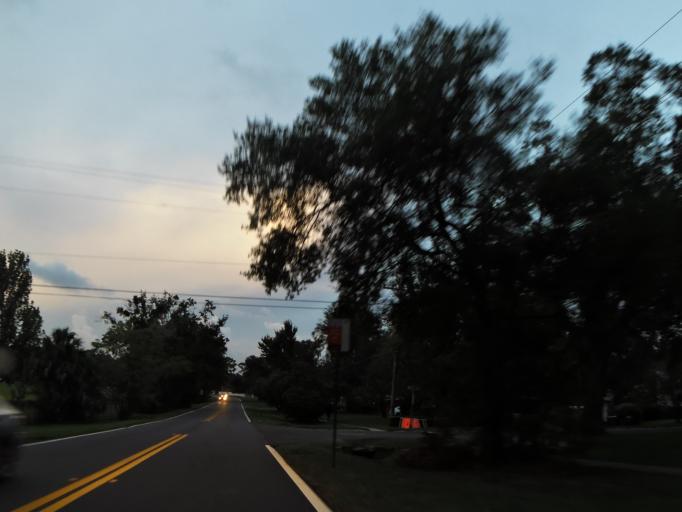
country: US
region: Florida
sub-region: Duval County
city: Jacksonville
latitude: 30.3747
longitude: -81.6072
